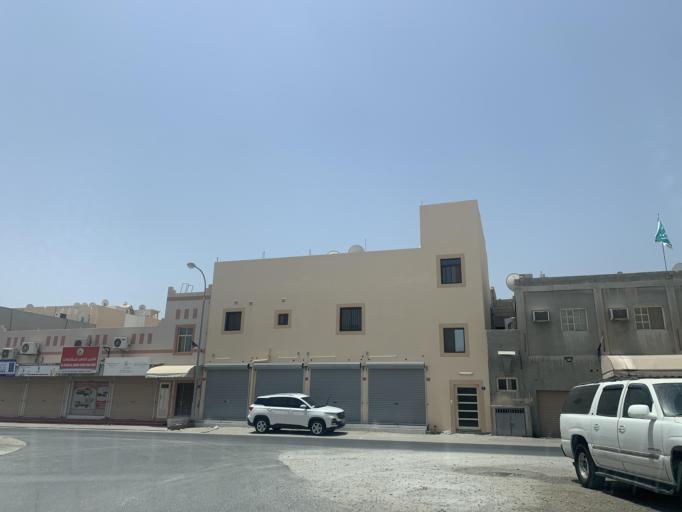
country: BH
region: Central Governorate
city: Madinat Hamad
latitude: 26.1456
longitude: 50.5015
